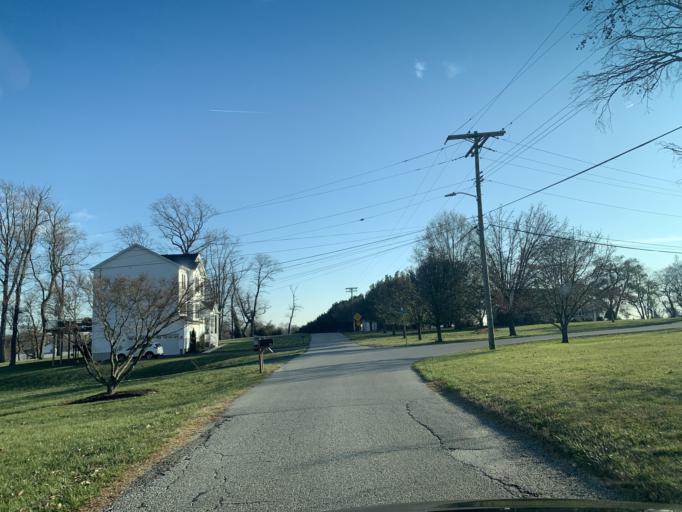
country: US
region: Maryland
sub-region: Baltimore County
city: Perry Hall
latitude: 39.4297
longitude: -76.4544
